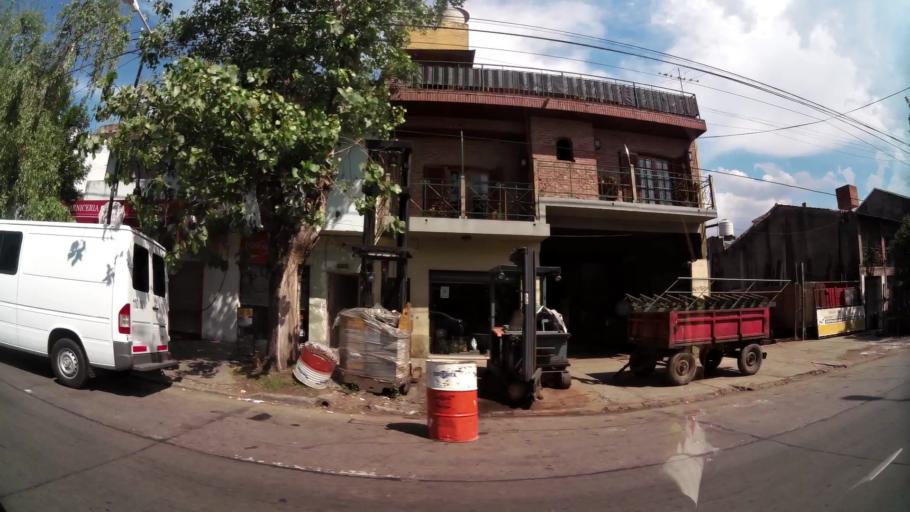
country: AR
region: Buenos Aires
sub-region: Partido de Tigre
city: Tigre
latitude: -34.4708
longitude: -58.5938
